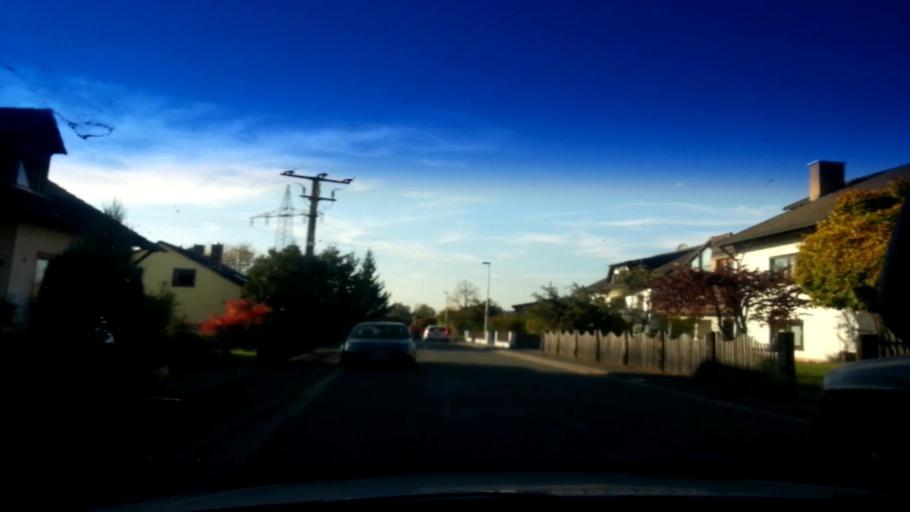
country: DE
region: Bavaria
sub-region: Upper Franconia
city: Litzendorf
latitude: 49.9128
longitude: 10.9967
